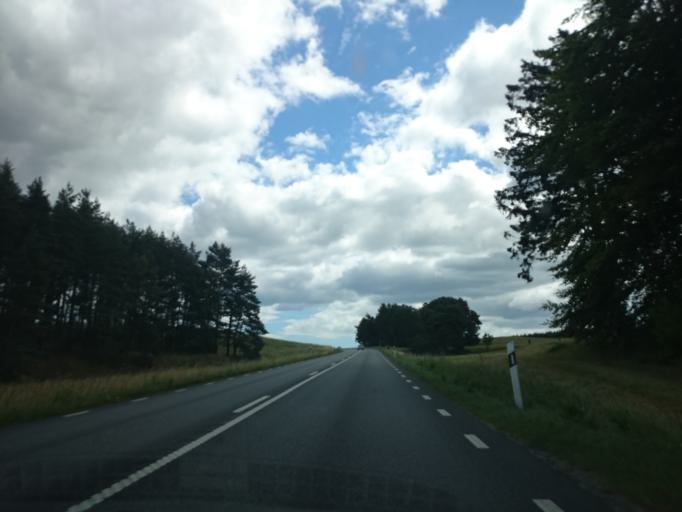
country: SE
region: Skane
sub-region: Kristianstads Kommun
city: Degeberga
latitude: 55.8249
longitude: 14.1045
